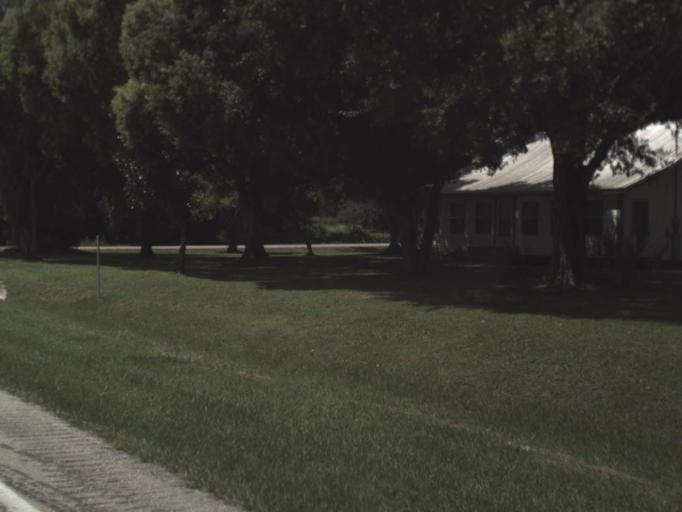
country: US
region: Florida
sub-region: Polk County
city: Mulberry
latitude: 27.7950
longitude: -81.9822
